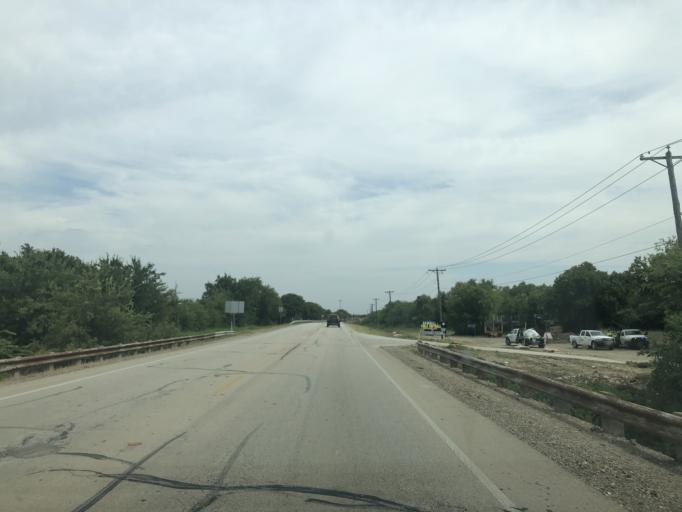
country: US
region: Texas
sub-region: Tarrant County
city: Blue Mound
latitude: 32.8910
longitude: -97.3466
